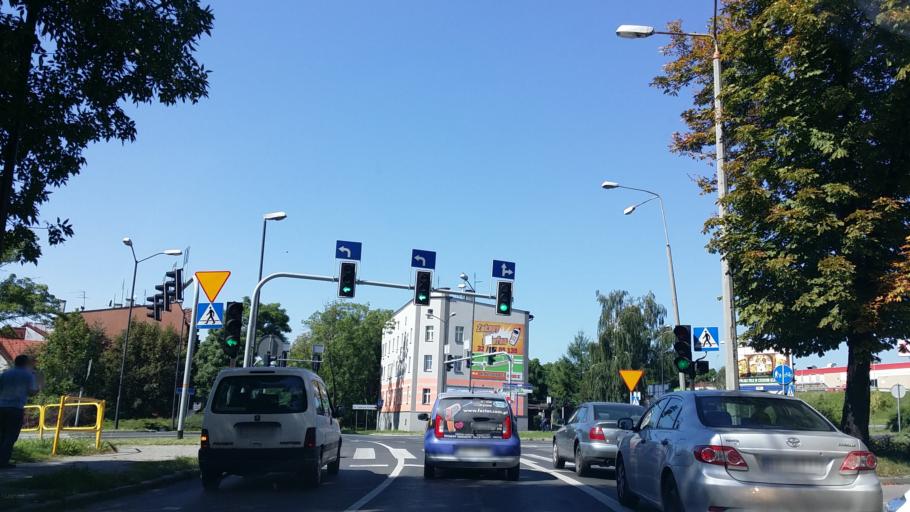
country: PL
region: Silesian Voivodeship
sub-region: Zabrze
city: Zabrze
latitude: 50.3105
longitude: 18.7757
